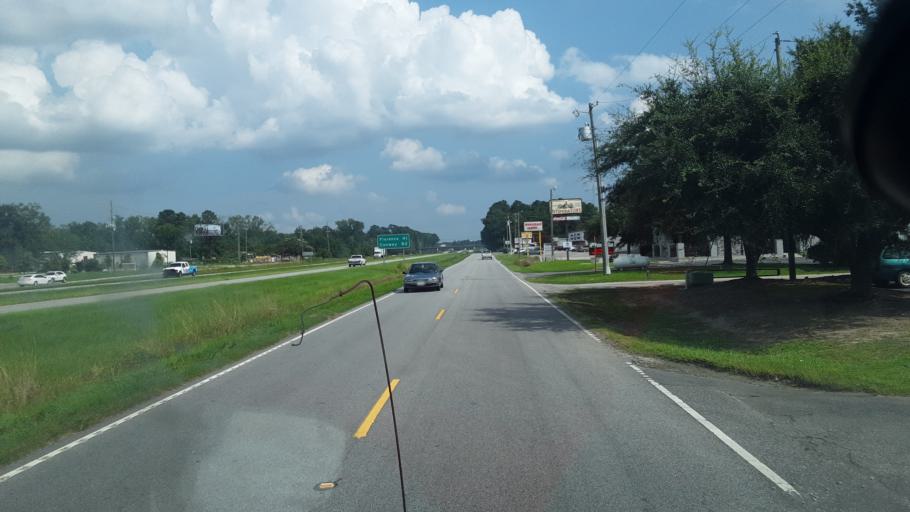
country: US
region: South Carolina
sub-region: Sumter County
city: Sumter
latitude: 33.9544
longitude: -80.3699
